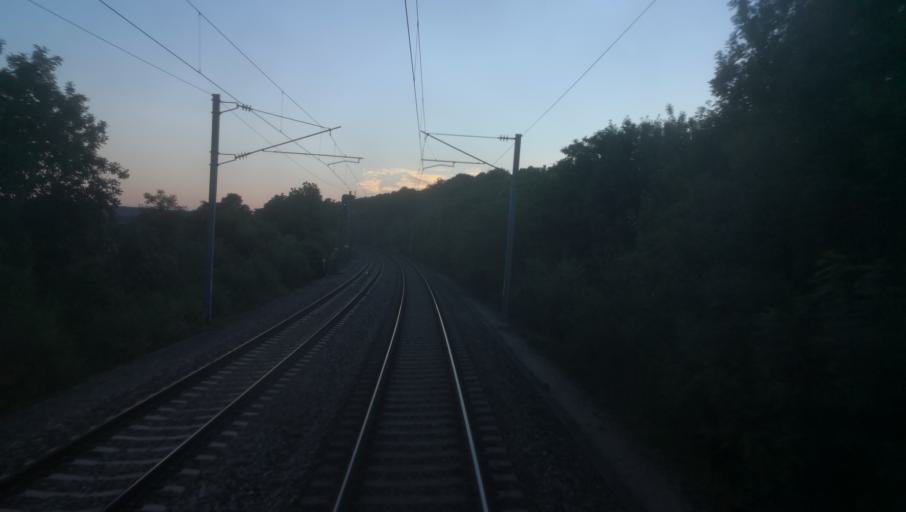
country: FR
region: Haute-Normandie
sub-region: Departement de l'Eure
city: Bueil
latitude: 48.9206
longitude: 1.4840
